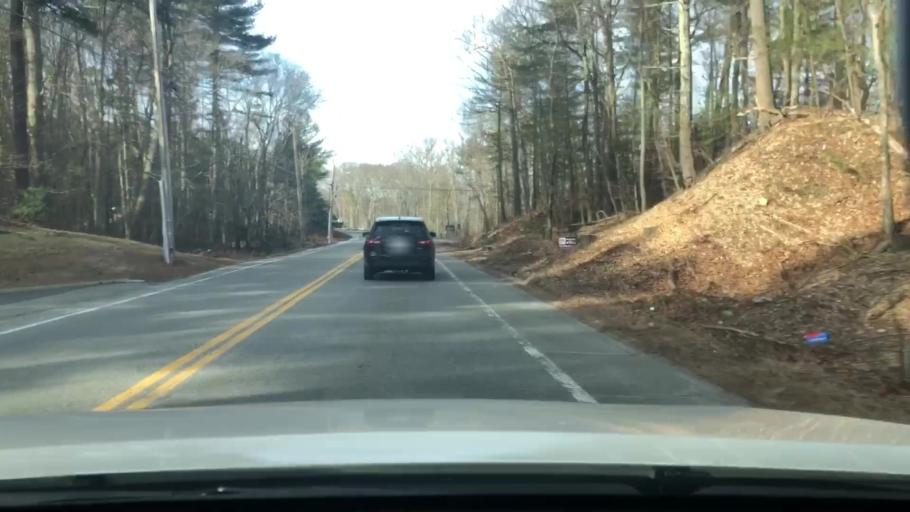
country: US
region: Massachusetts
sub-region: Worcester County
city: Grafton
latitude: 42.2005
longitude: -71.6580
